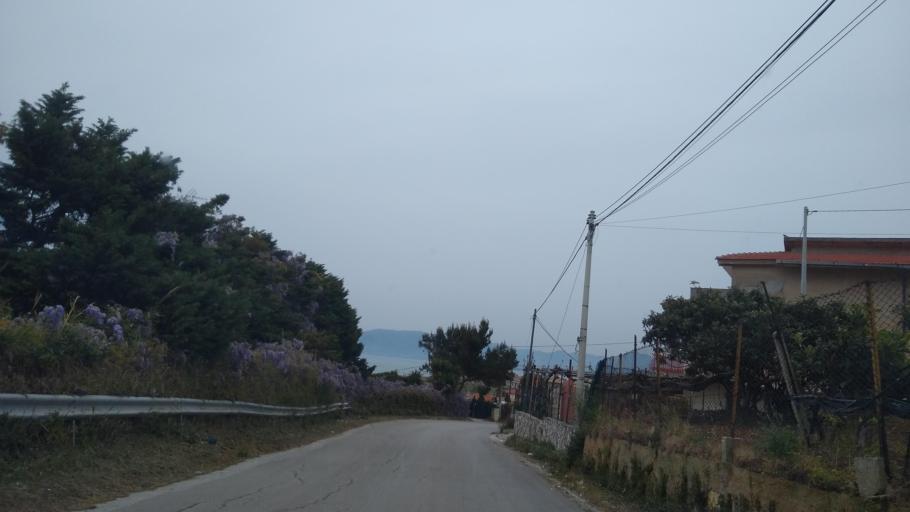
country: IT
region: Sicily
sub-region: Trapani
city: Castellammare del Golfo
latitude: 38.0216
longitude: 12.8995
